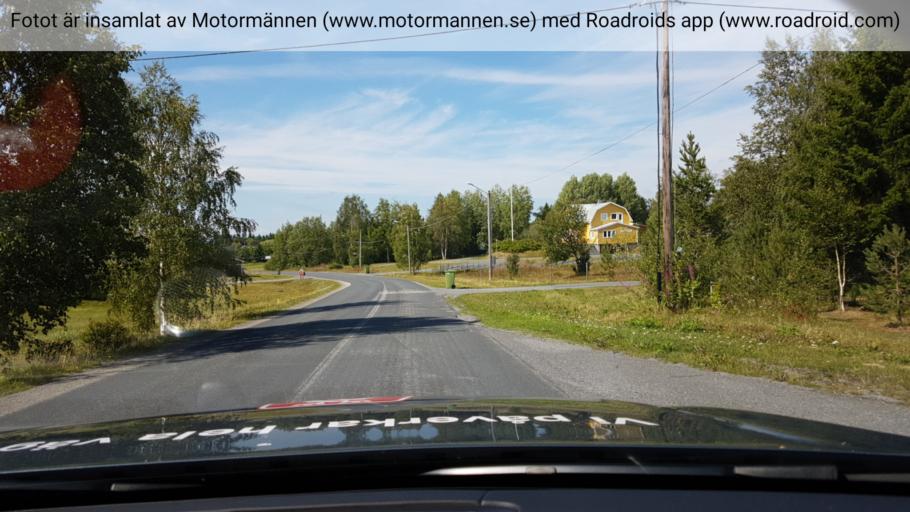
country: SE
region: Jaemtland
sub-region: Krokoms Kommun
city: Valla
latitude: 63.3035
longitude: 13.8701
